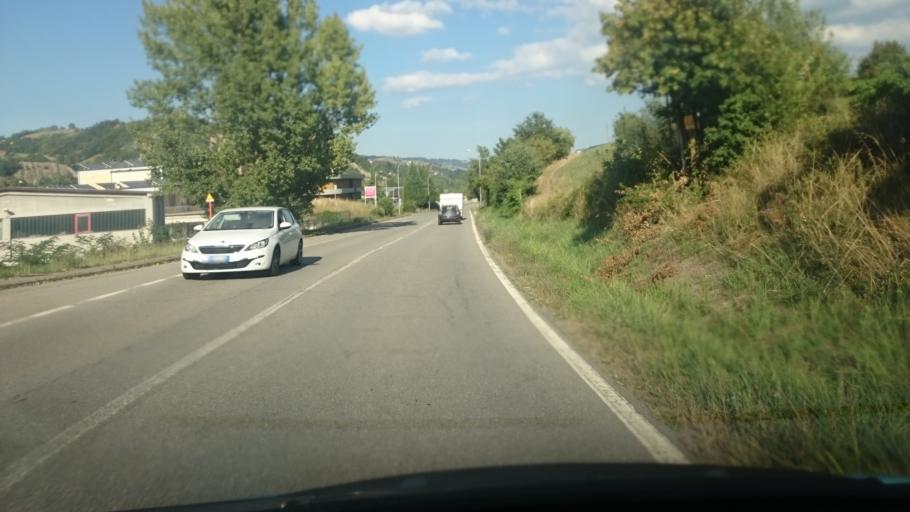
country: IT
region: Emilia-Romagna
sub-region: Provincia di Reggio Emilia
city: Villa Minozzo
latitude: 44.4030
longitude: 10.4798
